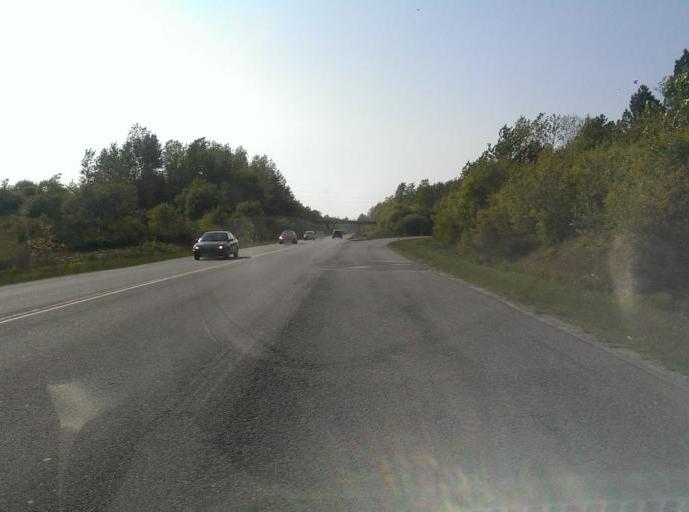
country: DK
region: South Denmark
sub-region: Esbjerg Kommune
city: Esbjerg
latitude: 55.5197
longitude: 8.4610
